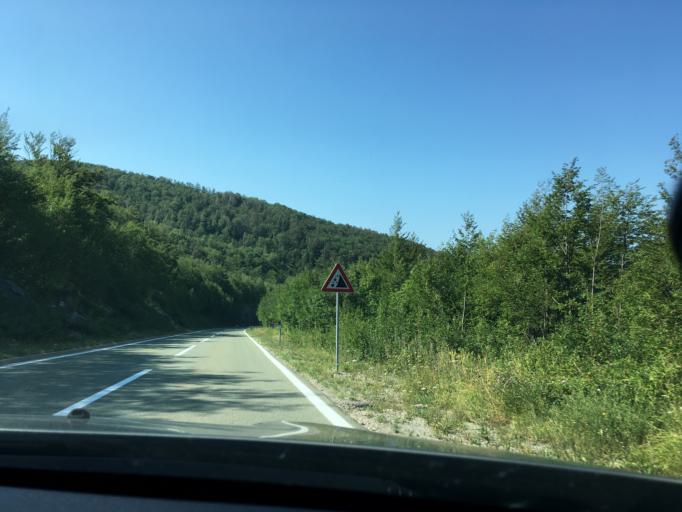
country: HR
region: Primorsko-Goranska
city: Hreljin
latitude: 45.3408
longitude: 14.6056
